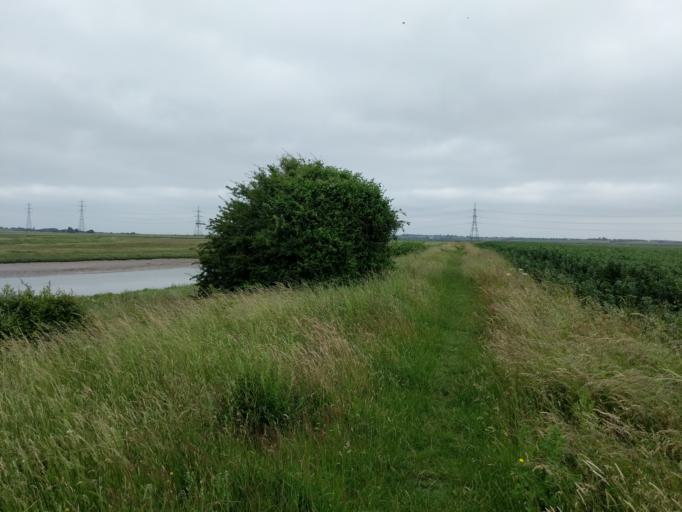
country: GB
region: England
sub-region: Kent
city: Faversham
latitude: 51.3324
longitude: 0.9133
